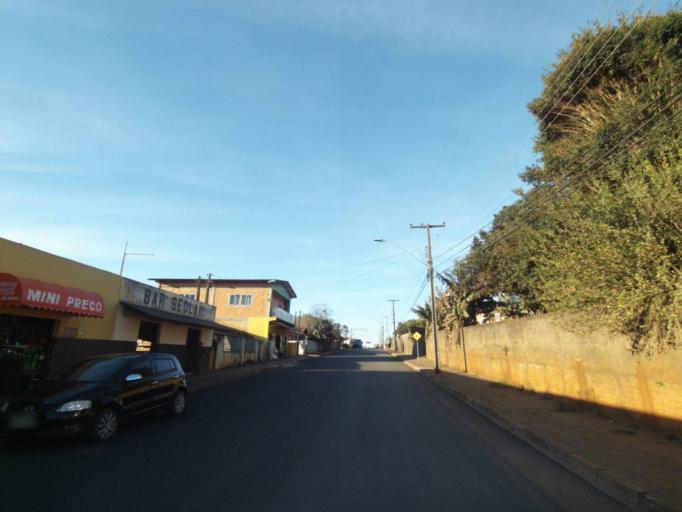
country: BR
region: Parana
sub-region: Tibagi
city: Tibagi
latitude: -24.5204
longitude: -50.4142
